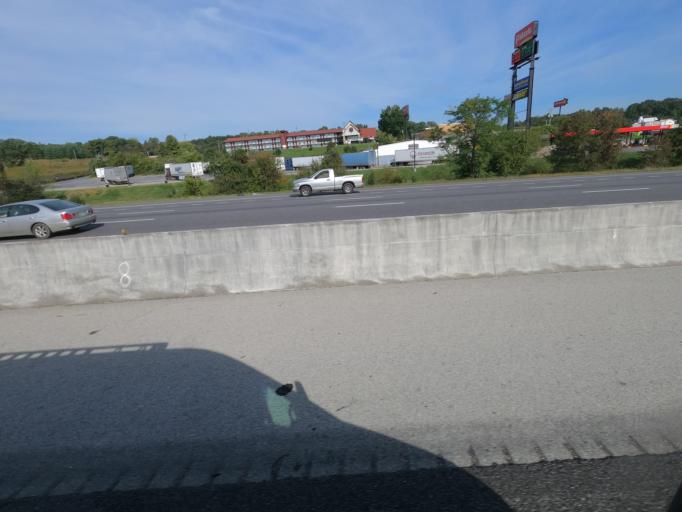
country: US
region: Tennessee
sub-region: Jefferson County
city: Dandridge
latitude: 36.0360
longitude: -83.4448
